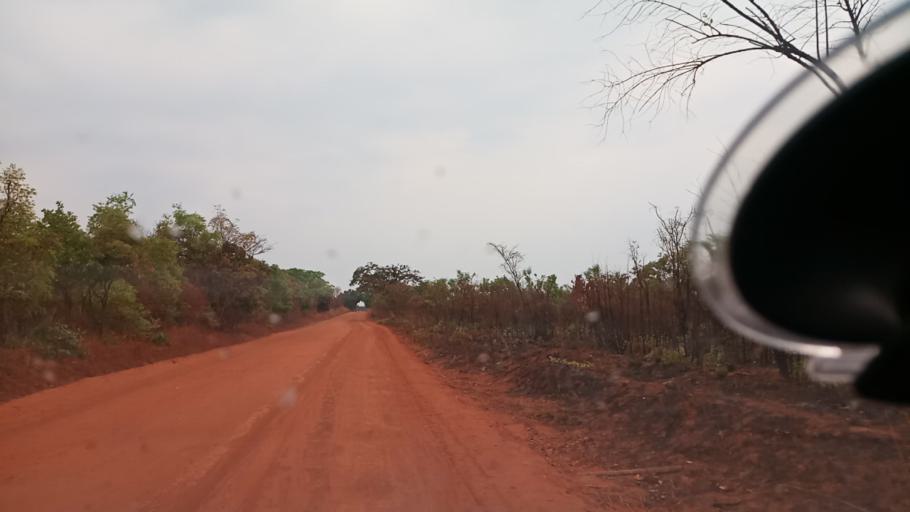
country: ZM
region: Luapula
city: Nchelenge
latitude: -9.1698
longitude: 28.2813
